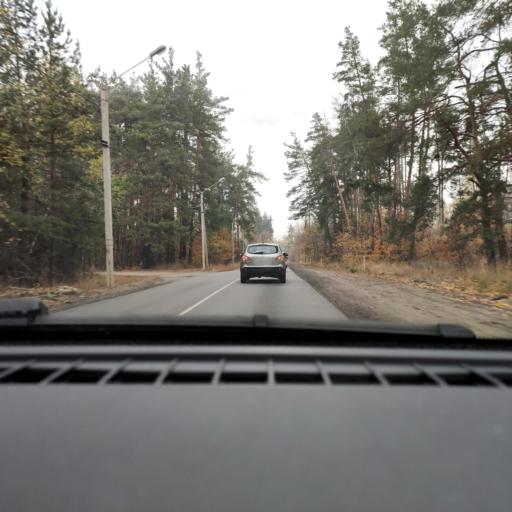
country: RU
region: Voronezj
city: Somovo
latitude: 51.7129
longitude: 39.3266
